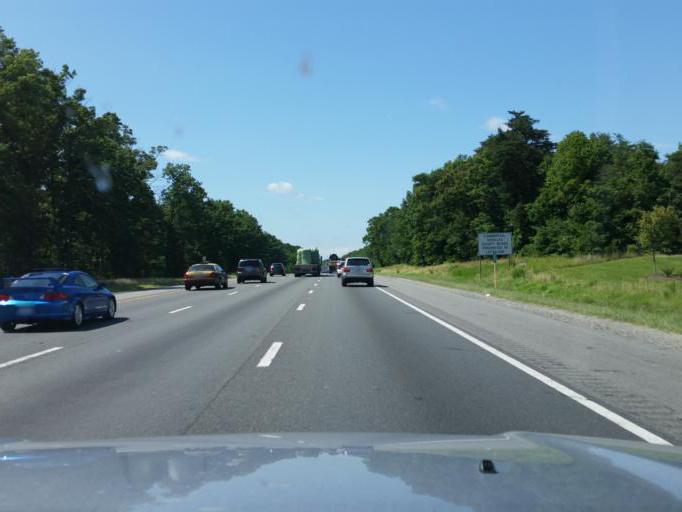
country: US
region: Virginia
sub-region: City of Fredericksburg
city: Fredericksburg
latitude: 38.2871
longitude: -77.5092
